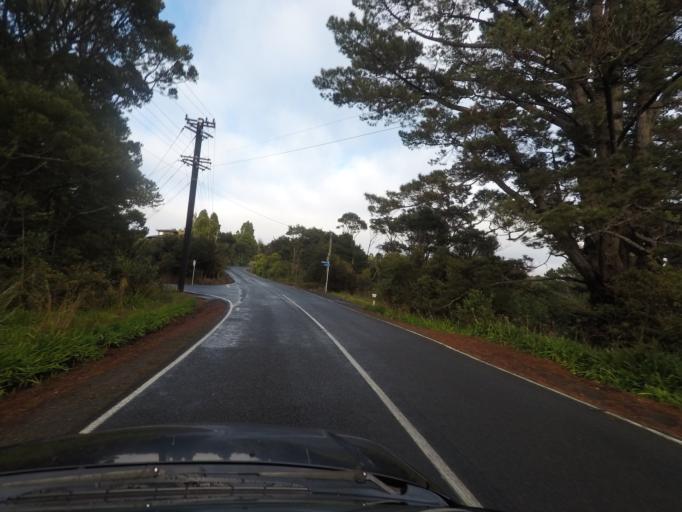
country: NZ
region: Auckland
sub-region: Auckland
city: Waitakere
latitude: -36.9146
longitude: 174.6023
